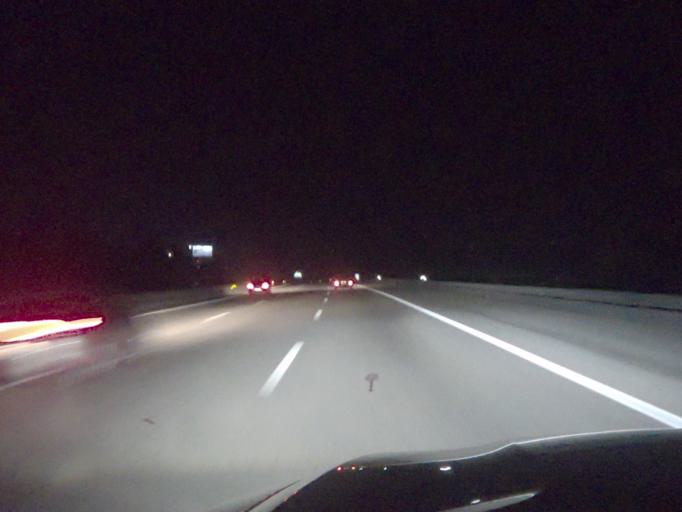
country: PT
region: Santarem
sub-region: Alcanena
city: Alcanena
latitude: 39.4389
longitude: -8.6279
